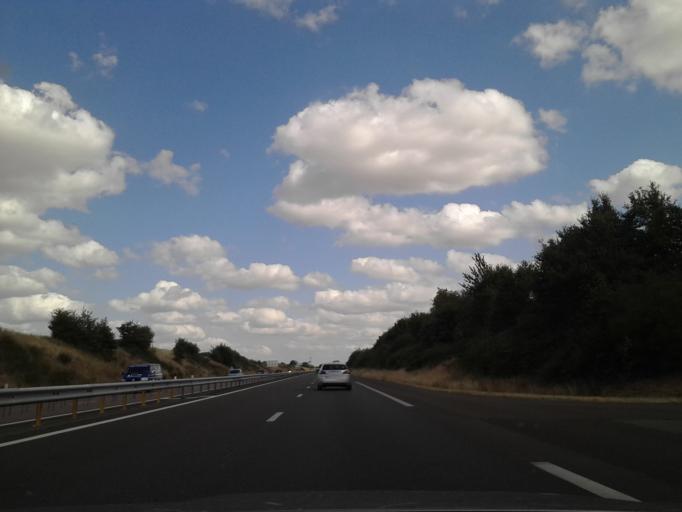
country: FR
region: Auvergne
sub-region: Departement de l'Allier
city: Vallon-en-Sully
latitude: 46.4977
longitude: 2.6506
